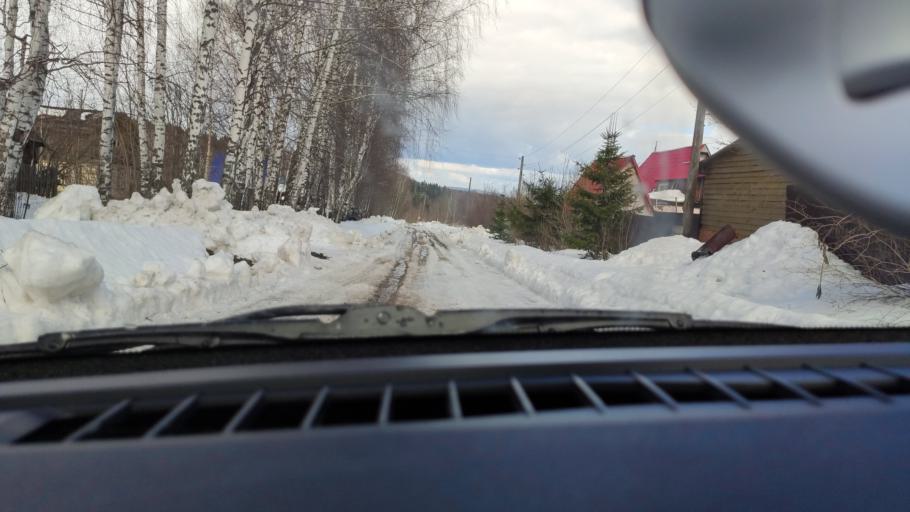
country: RU
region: Perm
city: Nytva
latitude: 57.9248
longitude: 55.4349
